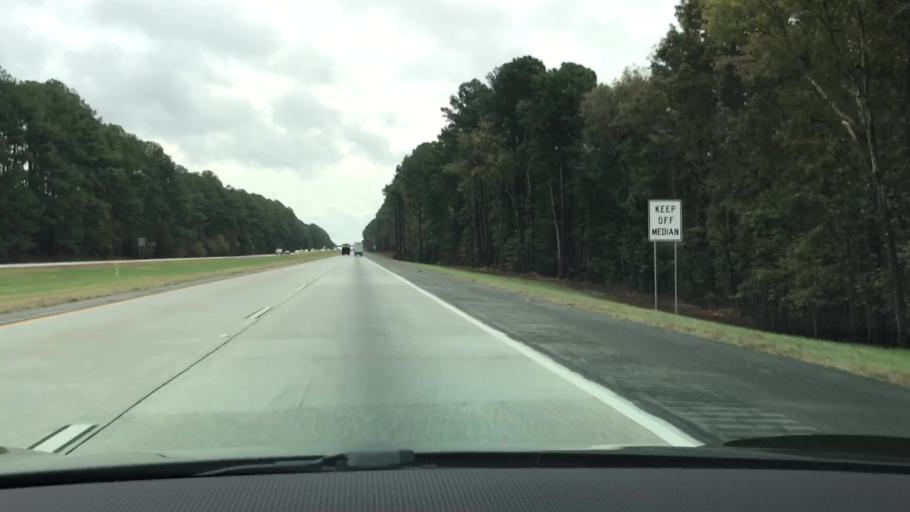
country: US
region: Georgia
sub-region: Taliaferro County
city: Crawfordville
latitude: 33.5169
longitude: -82.8595
